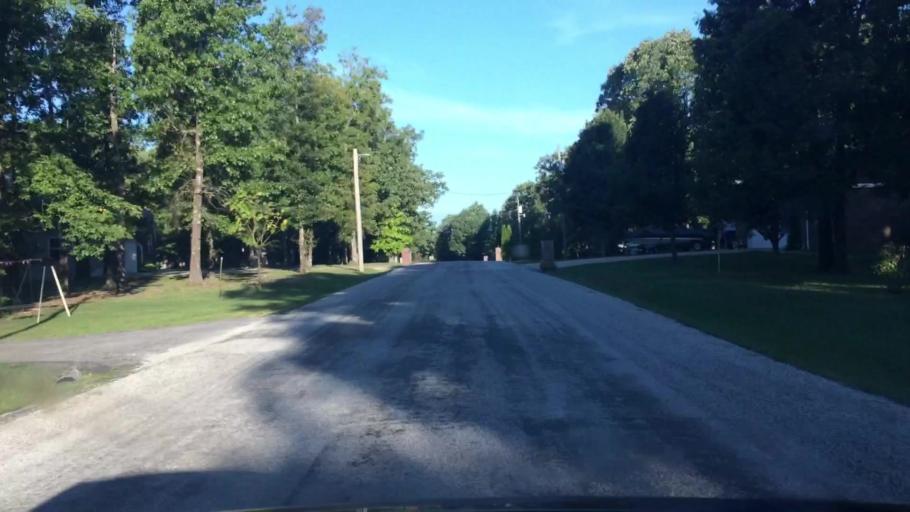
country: US
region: Missouri
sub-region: Greene County
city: Strafford
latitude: 37.2800
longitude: -93.0468
